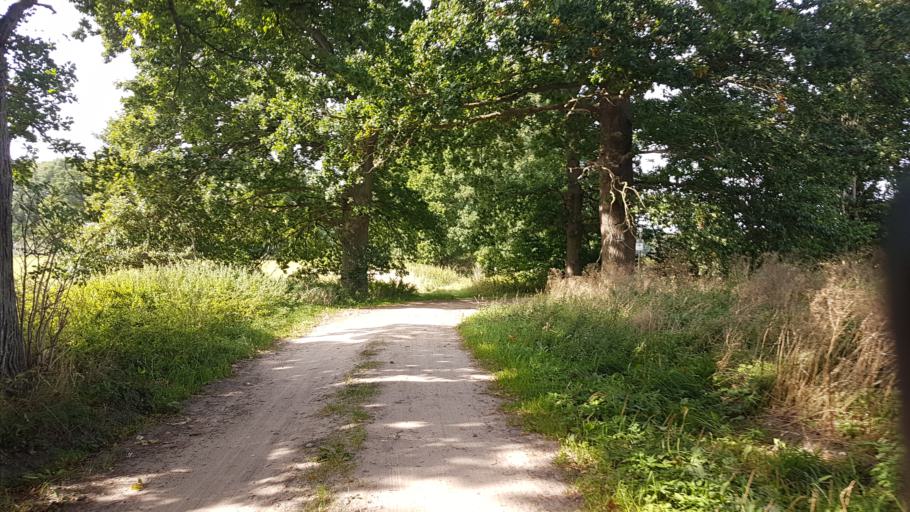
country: DE
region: Mecklenburg-Vorpommern
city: Samtens
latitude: 54.3915
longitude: 13.2602
